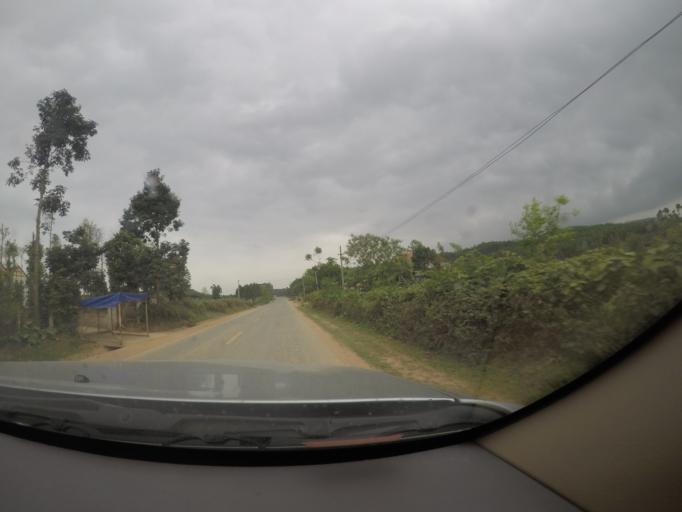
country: VN
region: Quang Binh
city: Ba Don
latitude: 17.6159
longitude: 106.3843
